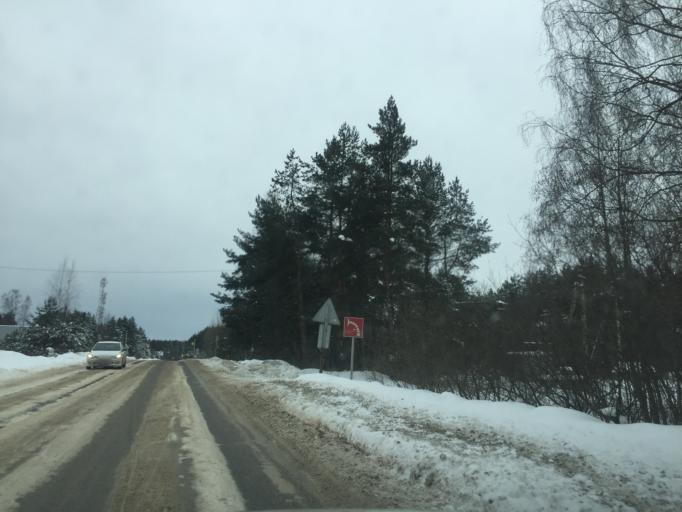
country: RU
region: Leningrad
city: Imeni Sverdlova
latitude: 59.8639
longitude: 30.6711
